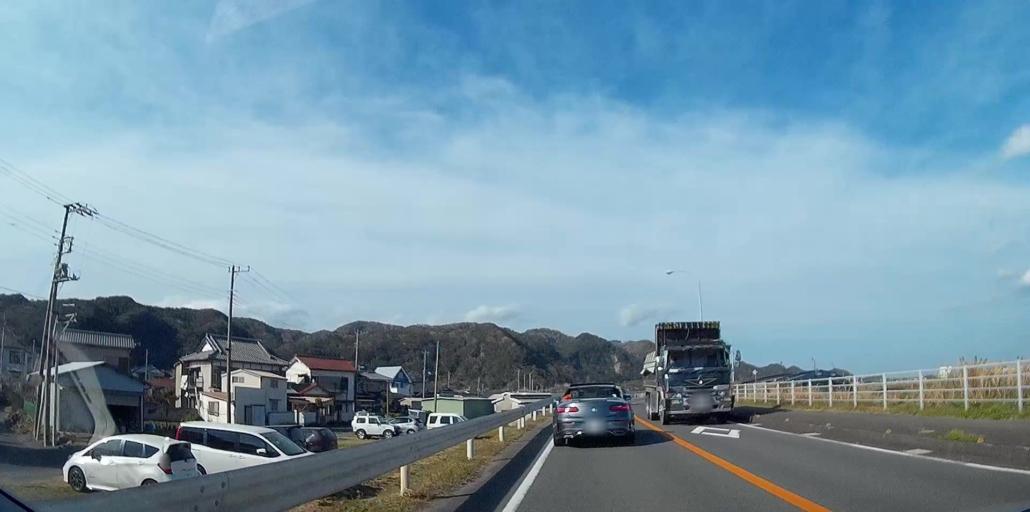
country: JP
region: Chiba
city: Tateyama
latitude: 34.9212
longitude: 139.9418
